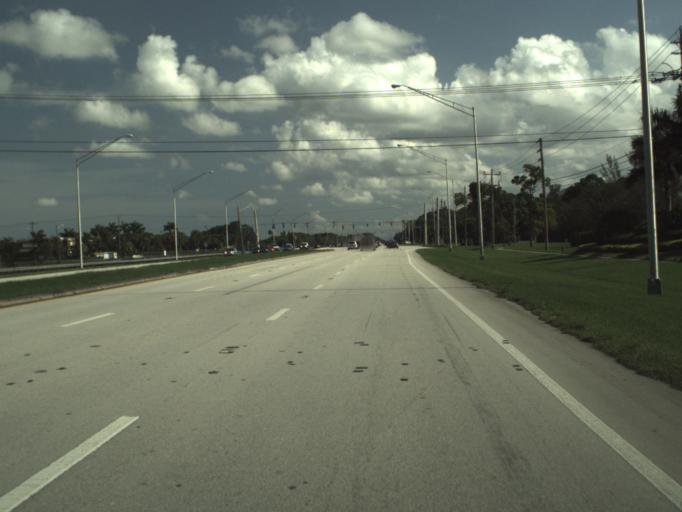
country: US
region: Florida
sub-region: Palm Beach County
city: Villages of Oriole
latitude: 26.4112
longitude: -80.2041
